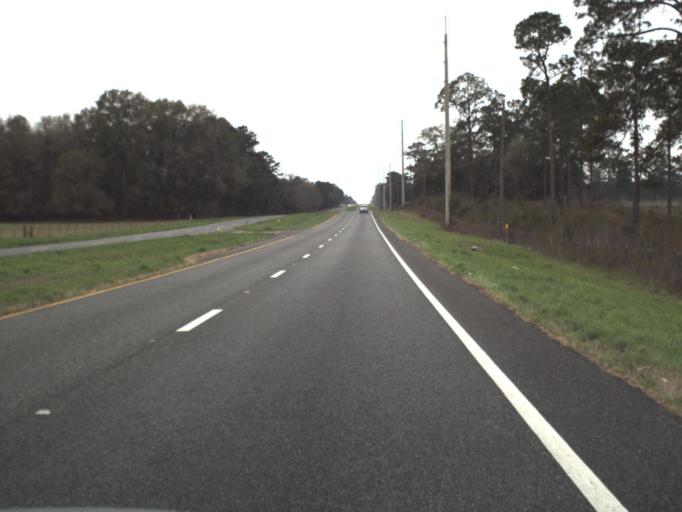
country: US
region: Florida
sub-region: Jefferson County
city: Monticello
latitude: 30.4077
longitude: -83.9877
